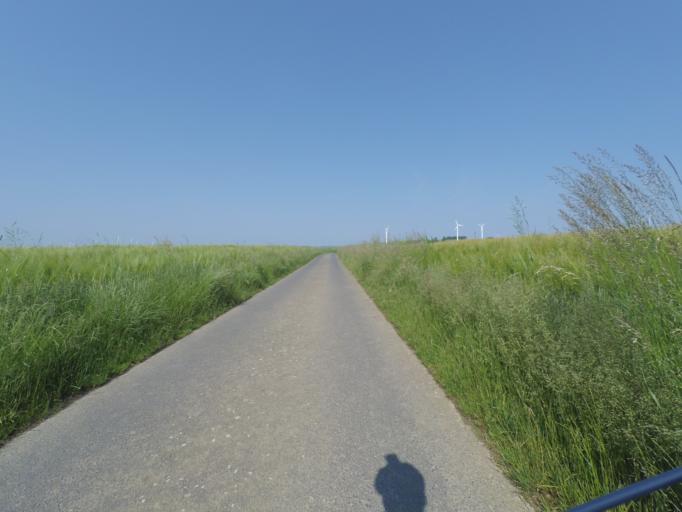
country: DE
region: Rheinland-Pfalz
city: Roes
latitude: 50.2345
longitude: 7.2585
